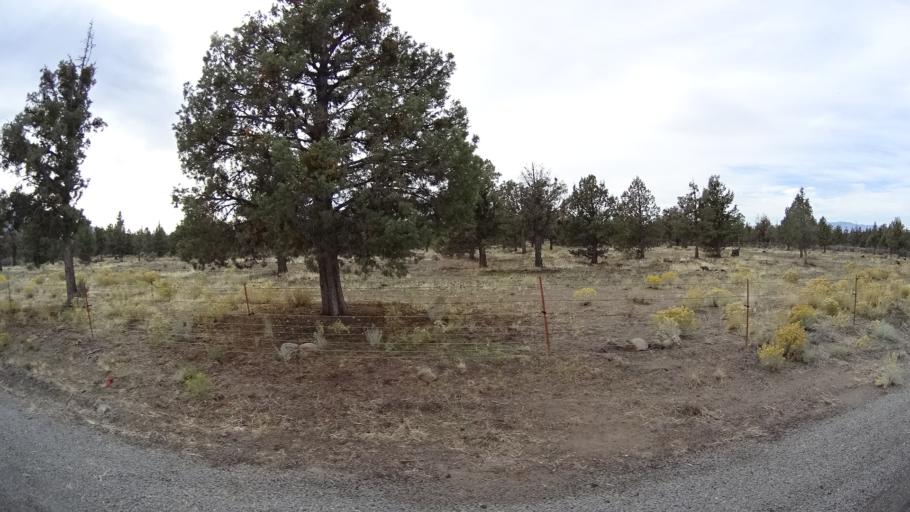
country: US
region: California
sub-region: Siskiyou County
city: Weed
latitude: 41.5869
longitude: -122.2989
